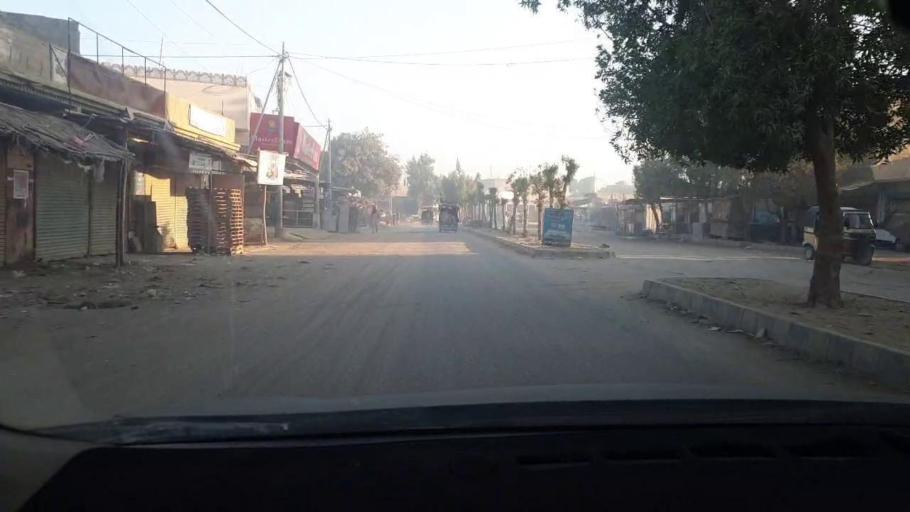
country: PK
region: Sindh
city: Malir Cantonment
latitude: 25.0092
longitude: 67.1583
